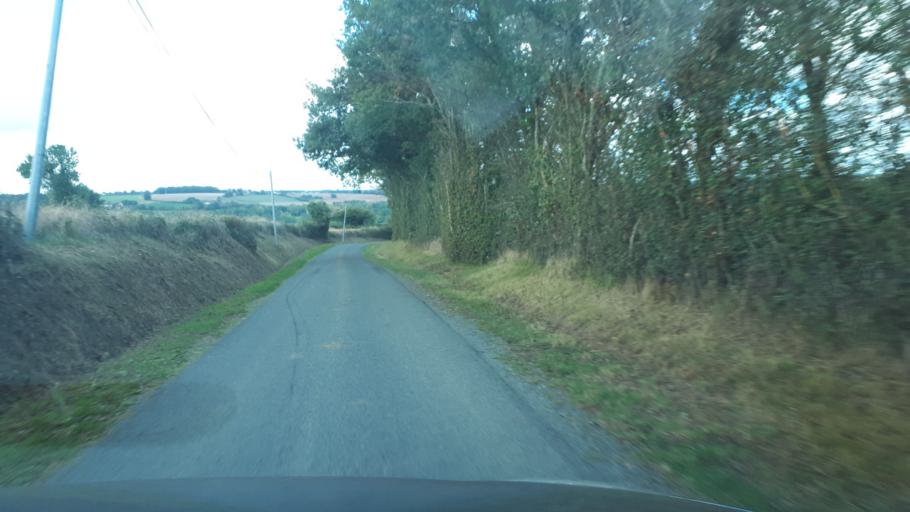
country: FR
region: Centre
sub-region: Departement du Loir-et-Cher
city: Sarge-sur-Braye
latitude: 47.9135
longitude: 0.8598
